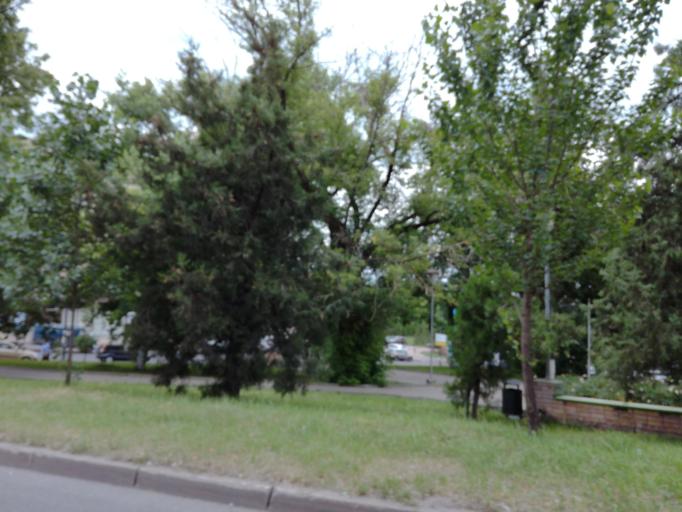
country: RU
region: Kursk
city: Kursk
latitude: 51.7297
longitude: 36.1909
